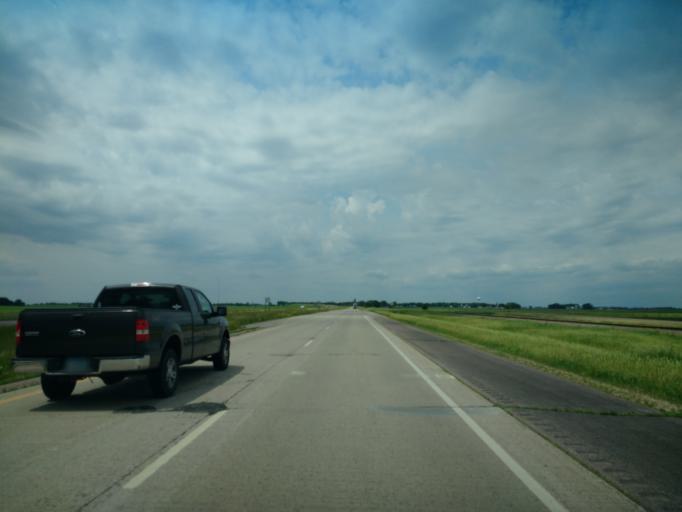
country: US
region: Minnesota
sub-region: Watonwan County
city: Saint James
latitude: 43.9628
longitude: -94.7563
